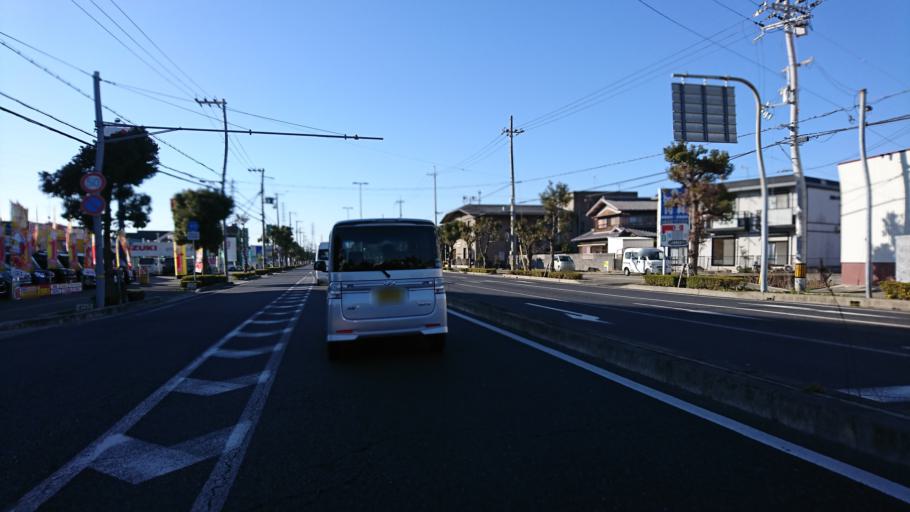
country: JP
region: Hyogo
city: Kakogawacho-honmachi
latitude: 34.7795
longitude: 134.8141
